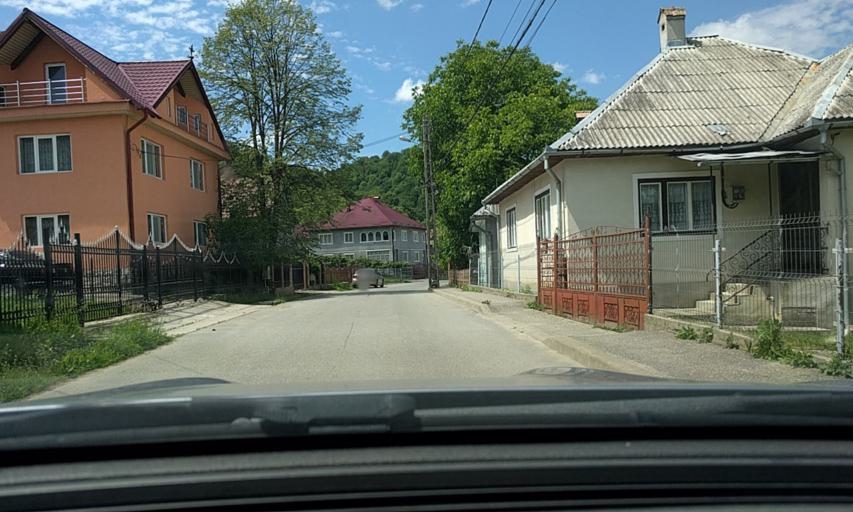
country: RO
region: Bistrita-Nasaud
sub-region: Oras Nasaud
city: Nasaud
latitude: 47.2773
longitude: 24.4086
